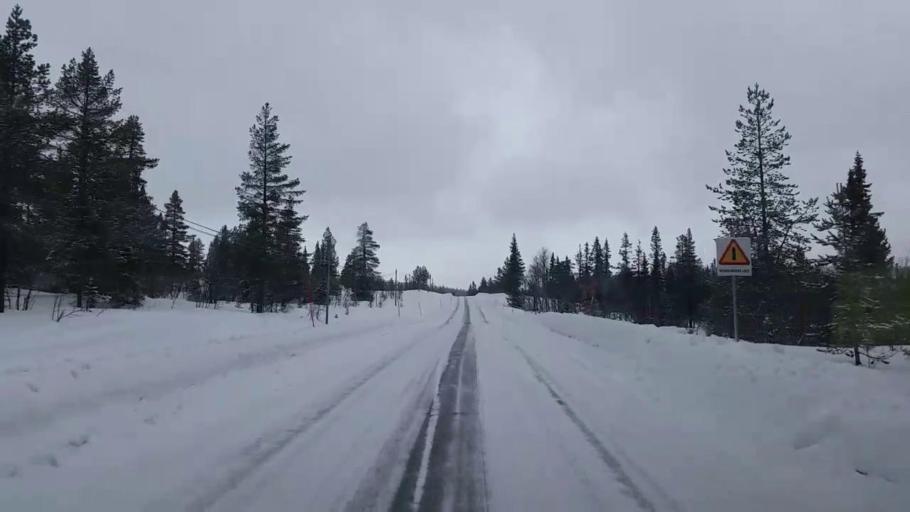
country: SE
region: Jaemtland
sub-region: Bergs Kommun
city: Hoverberg
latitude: 62.4924
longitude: 14.1161
